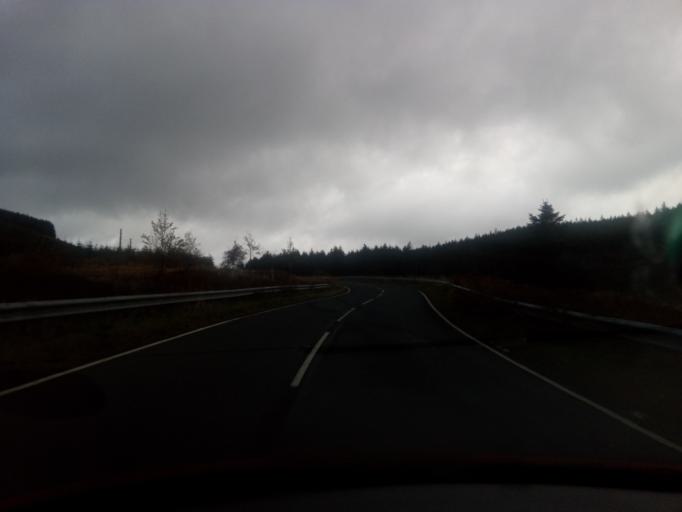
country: GB
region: Scotland
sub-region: The Scottish Borders
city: Hawick
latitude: 55.3150
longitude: -2.6535
